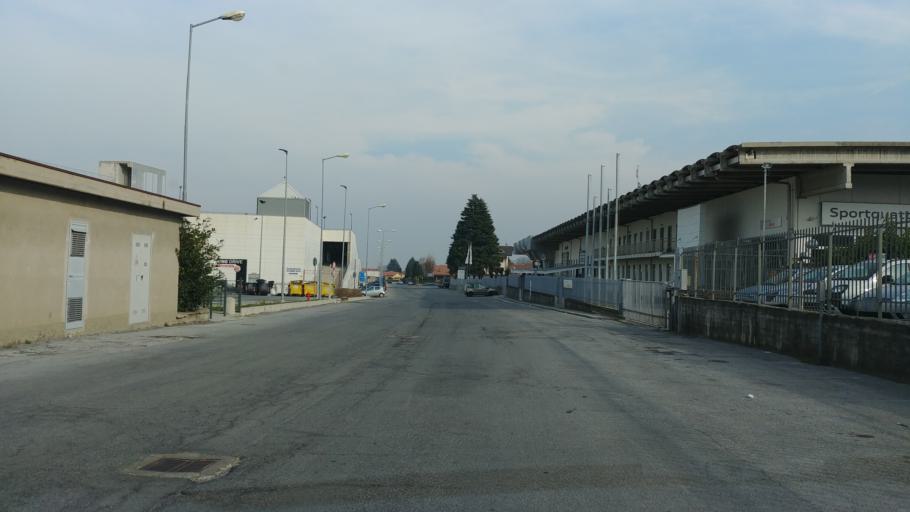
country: IT
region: Piedmont
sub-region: Provincia di Cuneo
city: Borgo San Dalmazzo
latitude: 44.3465
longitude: 7.5049
